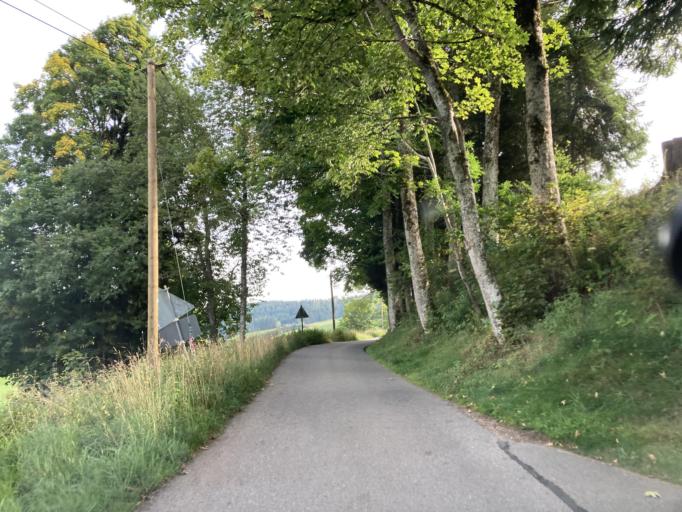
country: DE
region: Baden-Wuerttemberg
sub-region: Freiburg Region
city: Titisee-Neustadt
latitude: 47.9845
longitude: 8.1722
